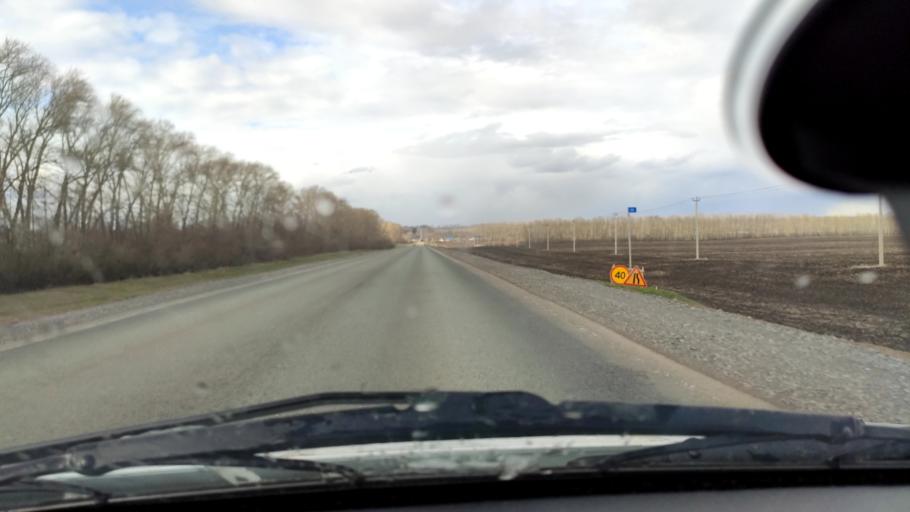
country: RU
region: Bashkortostan
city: Buzdyak
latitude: 54.6696
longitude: 54.5455
